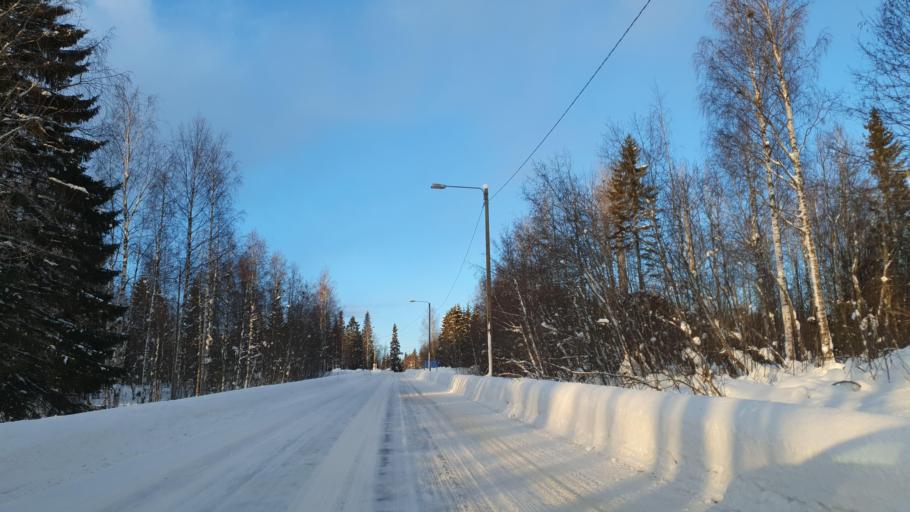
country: FI
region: Kainuu
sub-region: Kajaani
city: Ristijaervi
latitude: 64.3390
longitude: 28.0967
